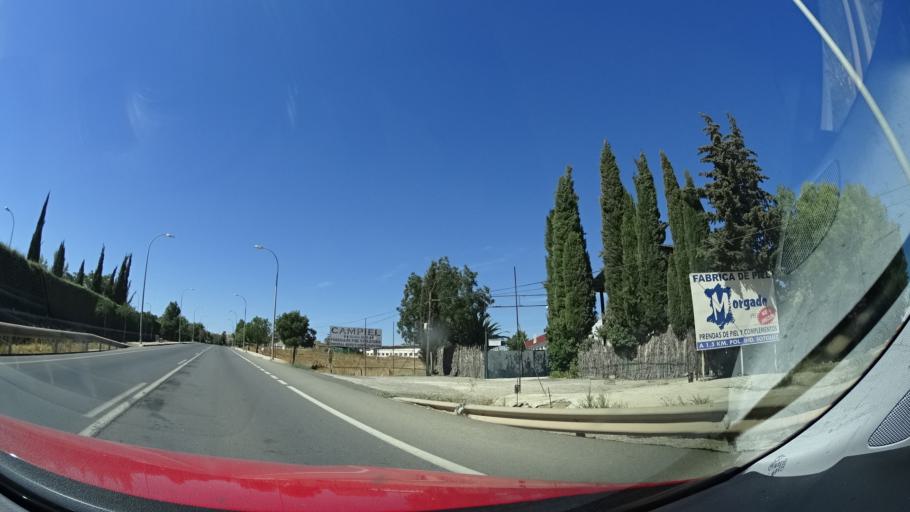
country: ES
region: Andalusia
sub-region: Provincia de Malaga
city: Campillos
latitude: 37.0509
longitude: -4.8562
